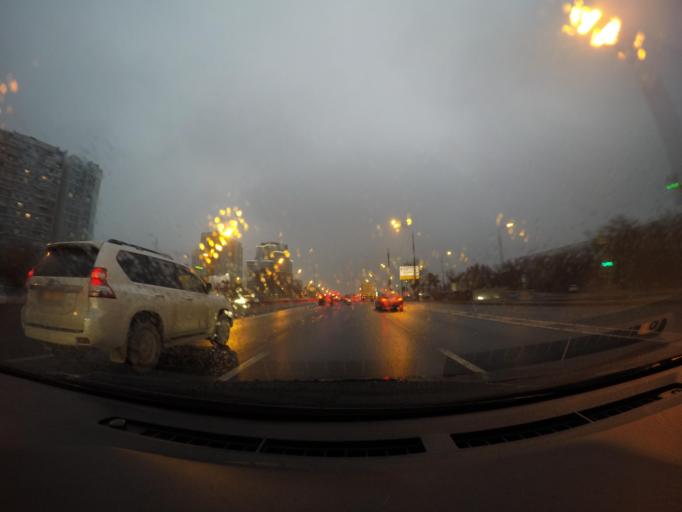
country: RU
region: Moscow
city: Nagornyy
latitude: 55.6280
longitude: 37.6177
